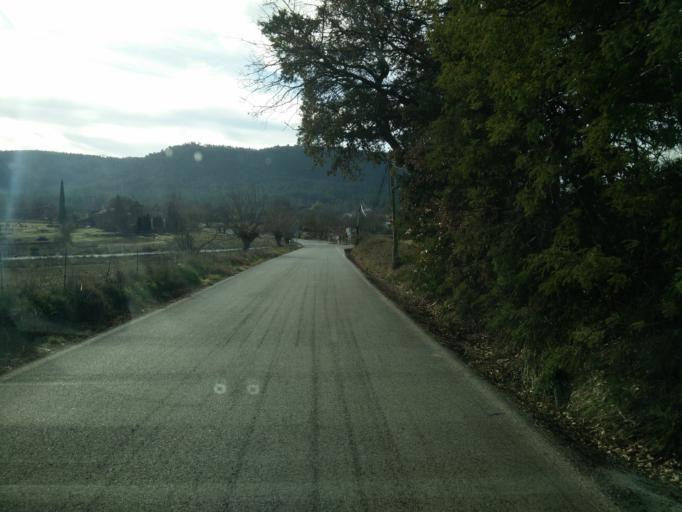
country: FR
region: Provence-Alpes-Cote d'Azur
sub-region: Departement du Var
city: Bagnols-en-Foret
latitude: 43.5384
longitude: 6.6898
